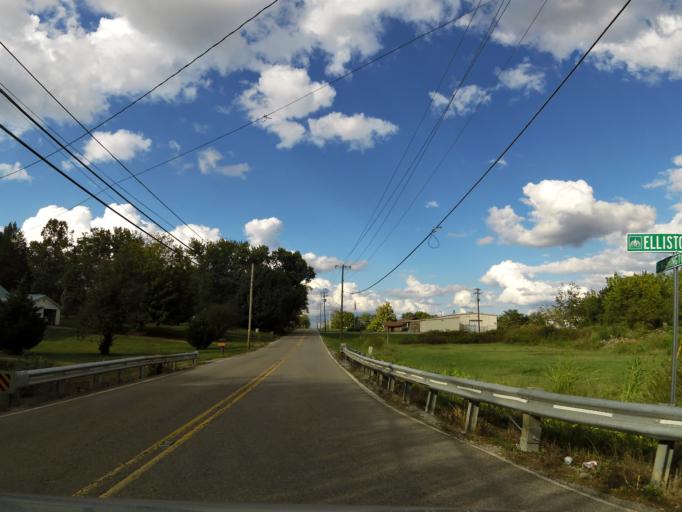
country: US
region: Tennessee
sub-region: Knox County
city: Mascot
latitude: 36.0824
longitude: -83.8237
